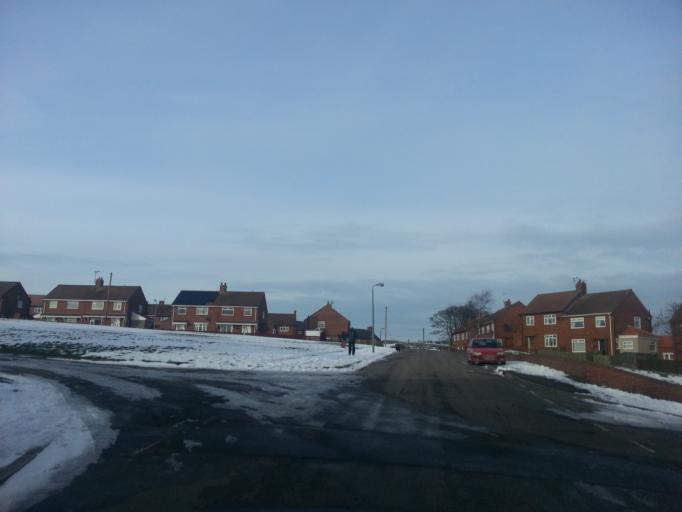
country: GB
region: England
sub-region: County Durham
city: Crook
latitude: 54.7166
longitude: -1.7581
